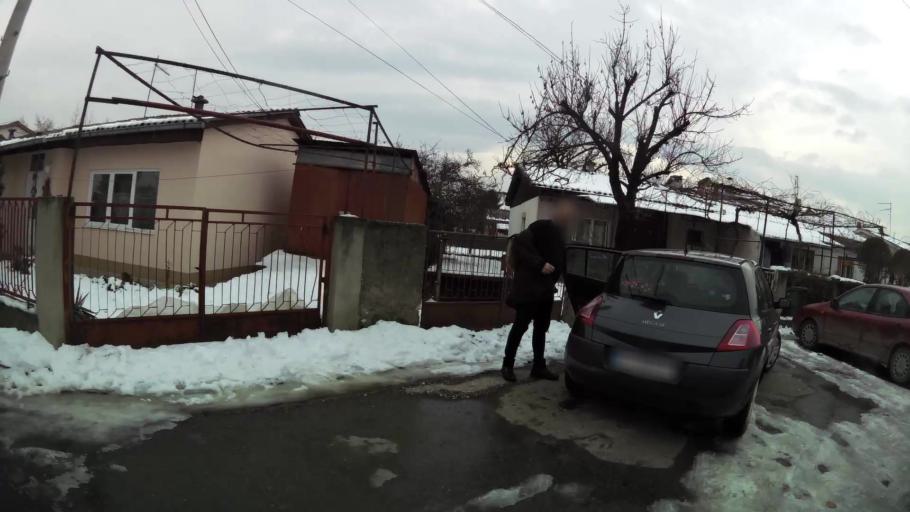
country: MK
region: Butel
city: Butel
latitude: 42.0343
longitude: 21.4434
